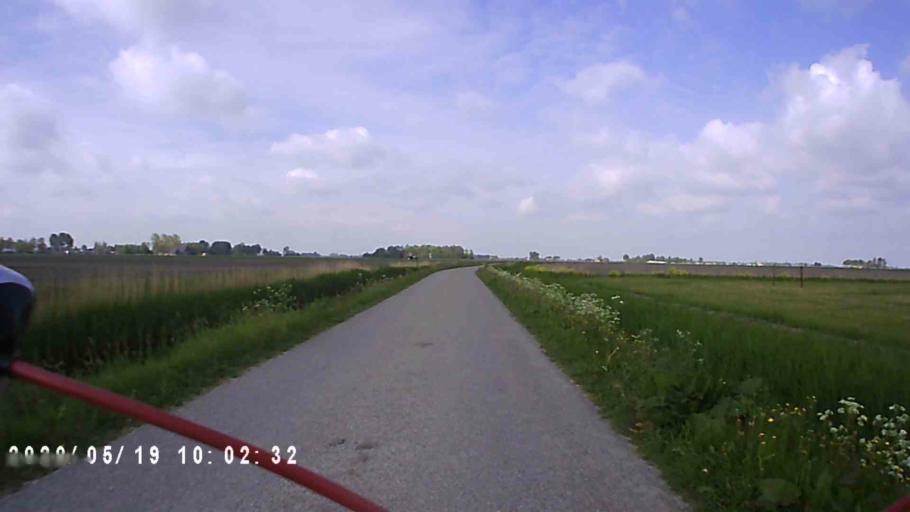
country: NL
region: Groningen
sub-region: Gemeente Zuidhorn
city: Grijpskerk
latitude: 53.3029
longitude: 6.2343
